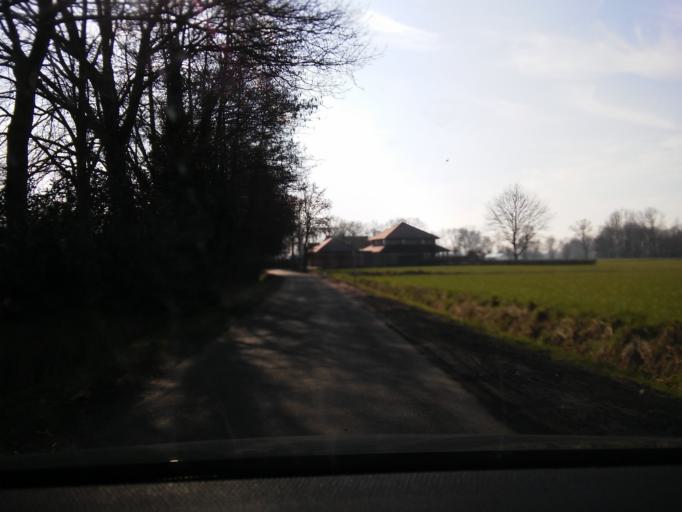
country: BE
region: Flanders
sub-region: Provincie Oost-Vlaanderen
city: Aalter
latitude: 51.0574
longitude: 3.4344
